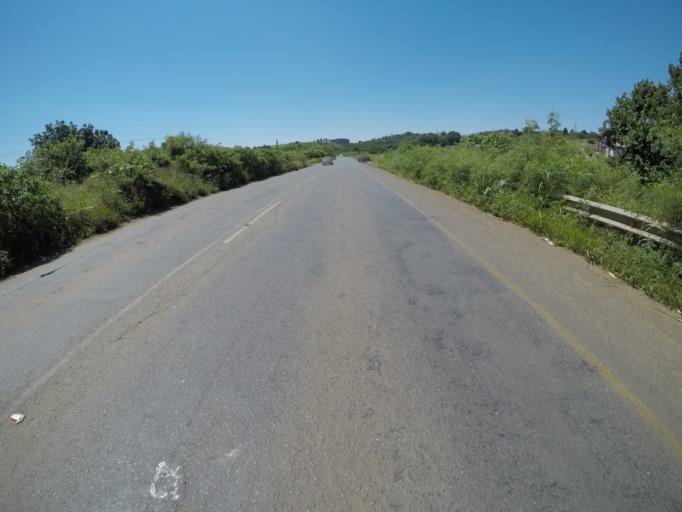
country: ZA
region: KwaZulu-Natal
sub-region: uThungulu District Municipality
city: Empangeni
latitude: -28.7507
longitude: 31.8783
